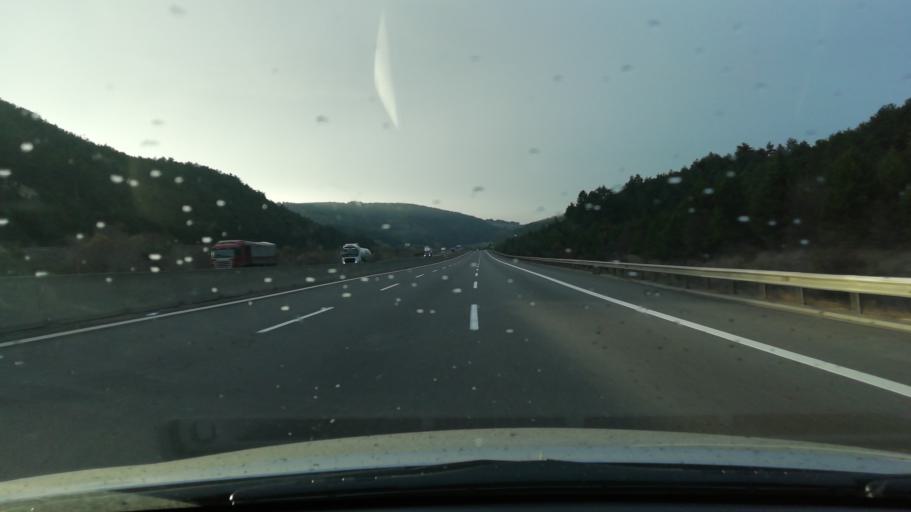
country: TR
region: Bolu
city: Bolu
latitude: 40.7352
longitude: 31.8025
